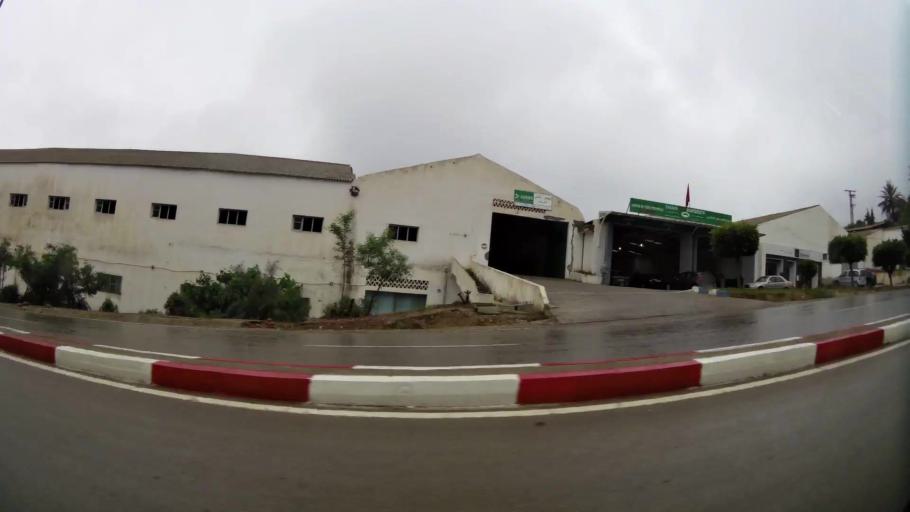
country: MA
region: Taza-Al Hoceima-Taounate
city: Al Hoceima
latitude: 35.2176
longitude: -3.9216
